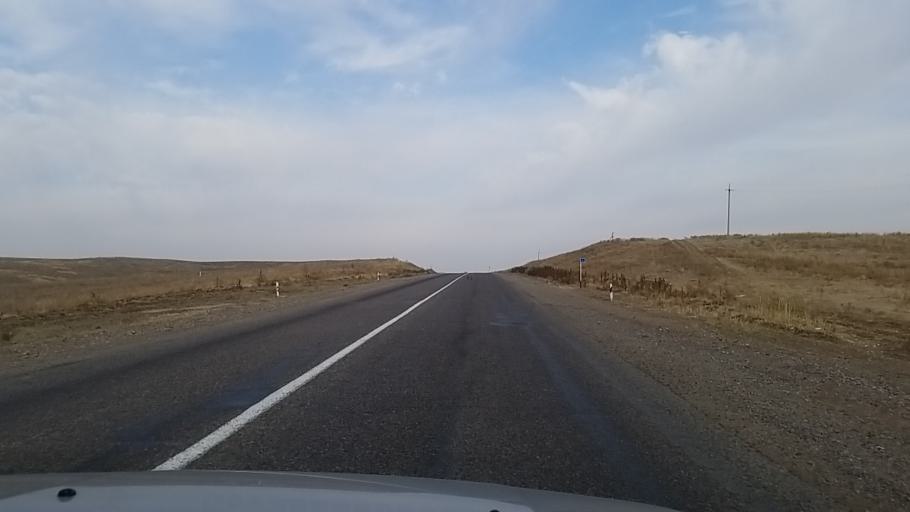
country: KZ
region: Almaty Oblysy
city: Burunday
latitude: 43.4935
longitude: 76.6639
